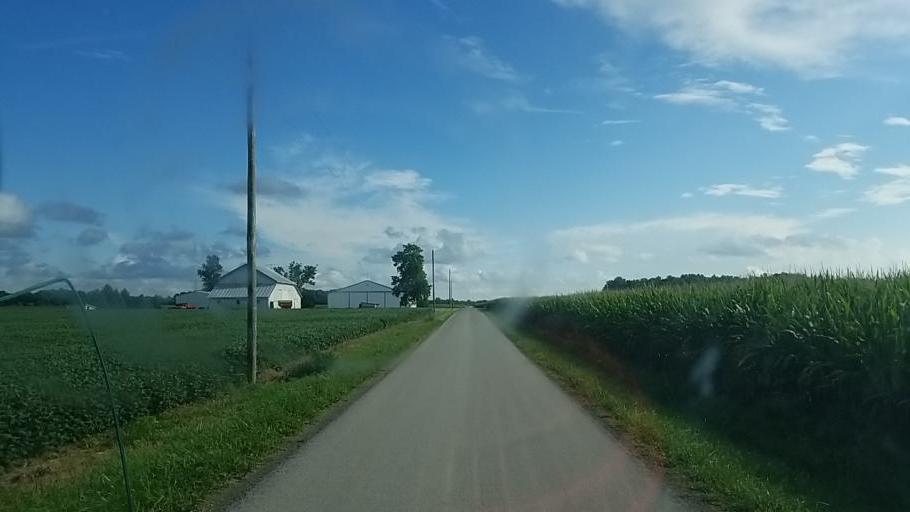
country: US
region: Ohio
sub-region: Wyandot County
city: Upper Sandusky
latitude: 40.7757
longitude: -83.3810
